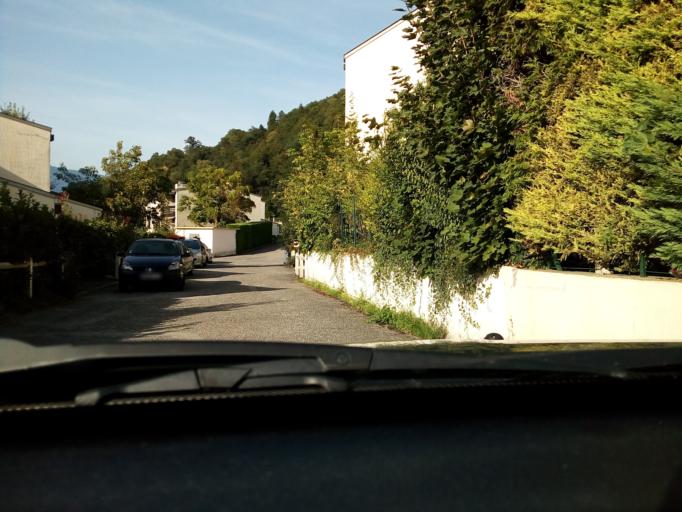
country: FR
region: Rhone-Alpes
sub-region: Departement de l'Isere
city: Saint-Martin-d'Heres
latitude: 45.1659
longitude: 5.7677
